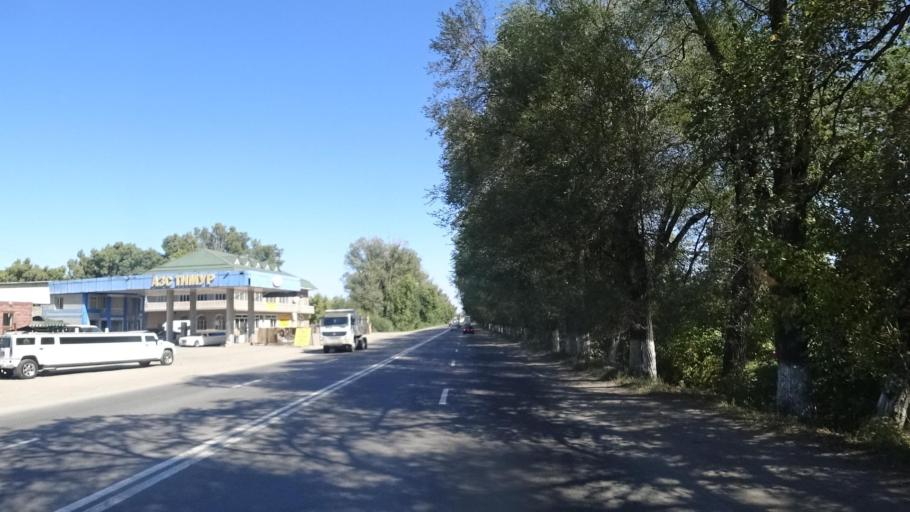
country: KZ
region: Almaty Oblysy
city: Energeticheskiy
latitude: 43.3300
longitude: 77.0344
